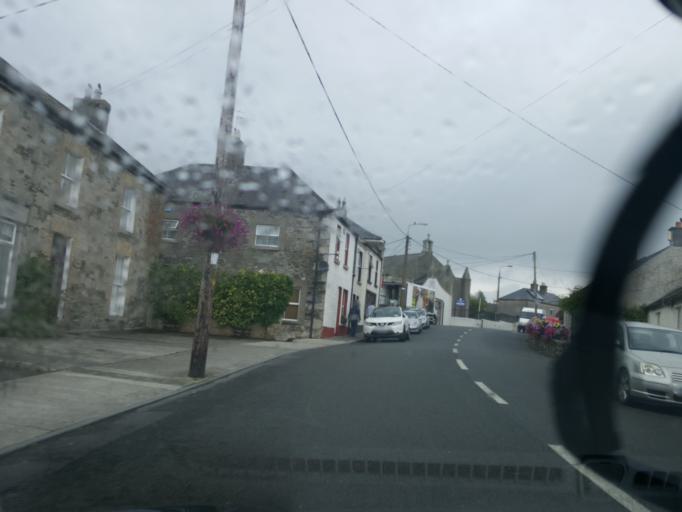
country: IE
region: Leinster
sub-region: Wicklow
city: Valleymount
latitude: 53.1311
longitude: -6.6168
